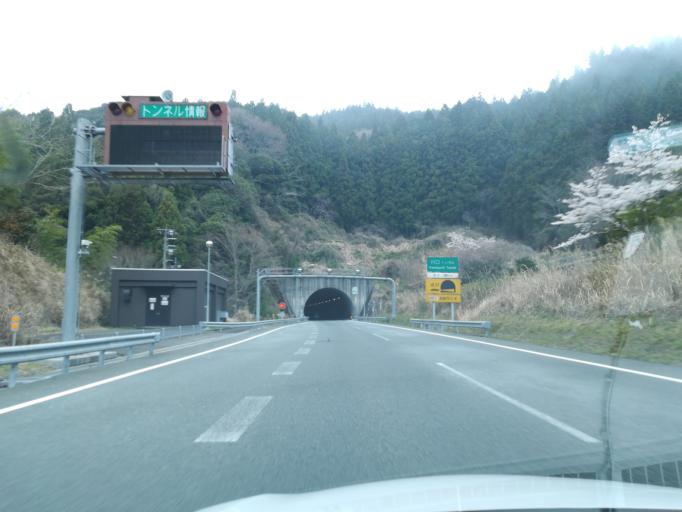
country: JP
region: Kochi
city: Kochi-shi
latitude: 33.7727
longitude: 133.6604
